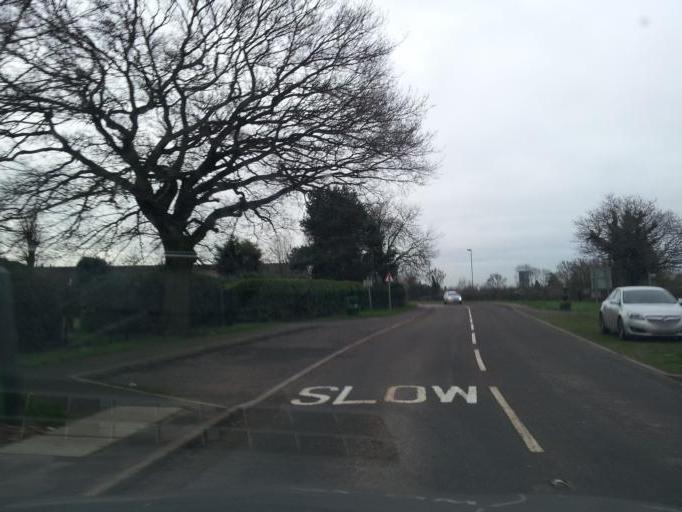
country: GB
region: England
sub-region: Derbyshire
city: Repton
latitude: 52.8562
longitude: -1.5643
